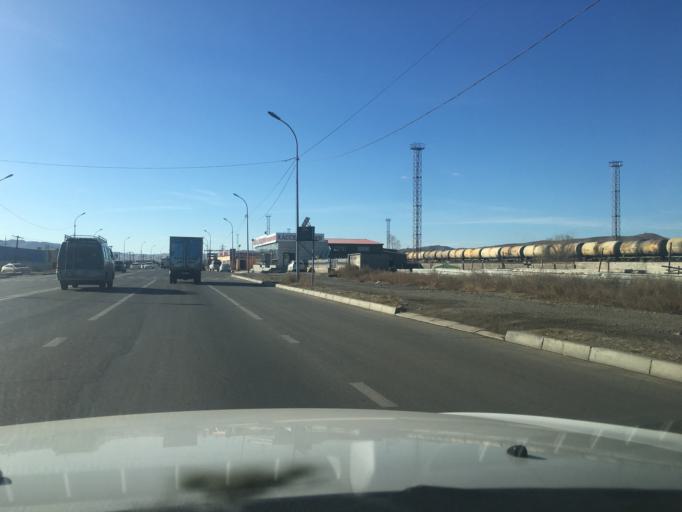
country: MN
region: Ulaanbaatar
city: Ulaanbaatar
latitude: 47.9052
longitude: 106.7596
